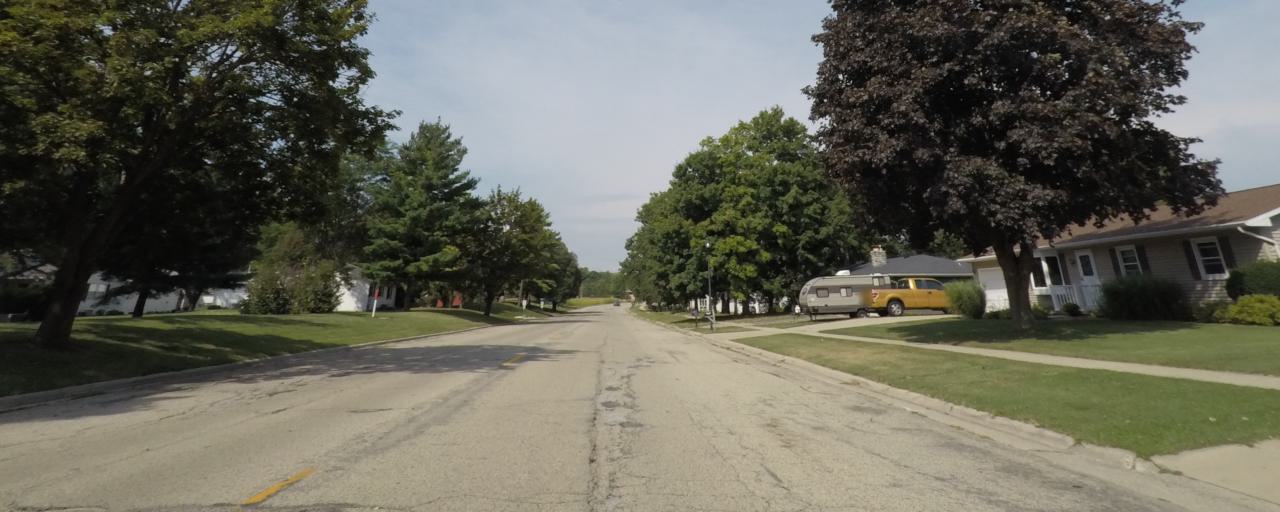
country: US
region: Wisconsin
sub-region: Jefferson County
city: Jefferson
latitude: 42.9902
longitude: -88.8194
